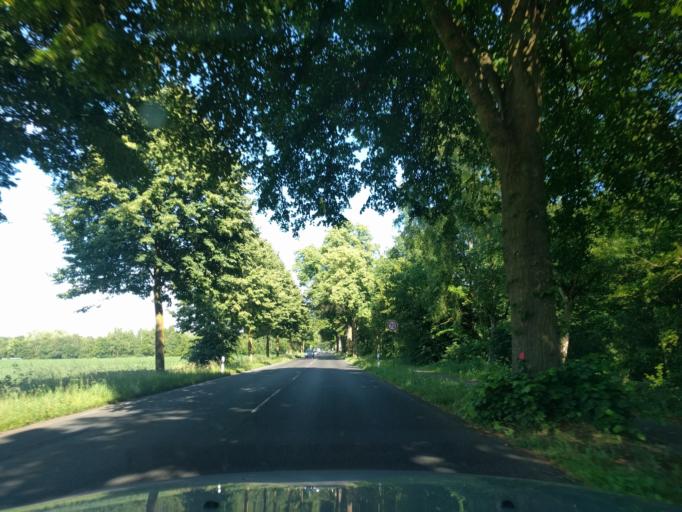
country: DE
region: North Rhine-Westphalia
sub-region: Regierungsbezirk Dusseldorf
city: Willich
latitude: 51.2283
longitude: 6.5716
